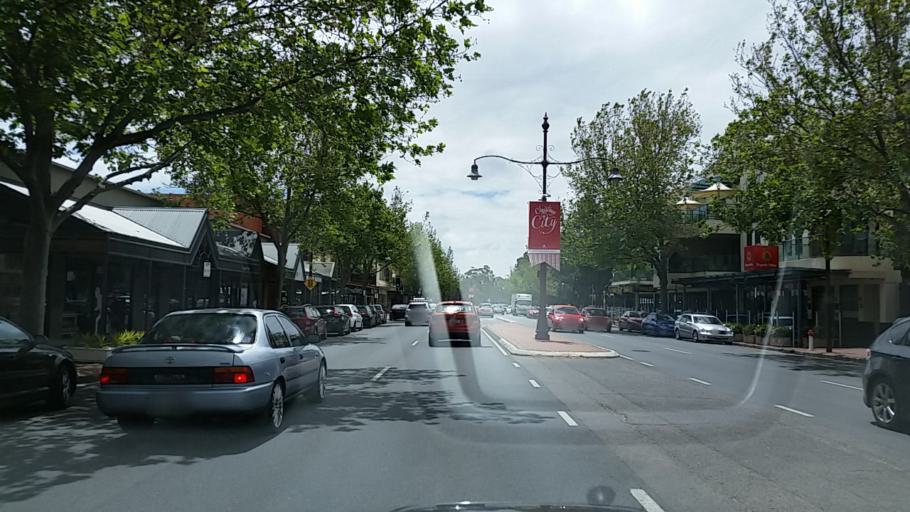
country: AU
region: South Australia
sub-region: Adelaide
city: North Adelaide
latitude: -34.9041
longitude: 138.5952
